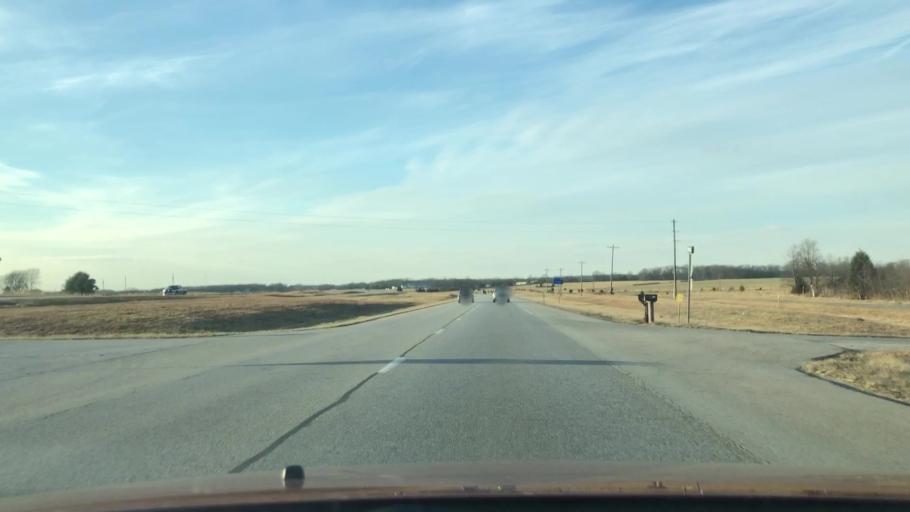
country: US
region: Missouri
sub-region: Webster County
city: Seymour
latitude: 37.1210
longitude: -92.6968
